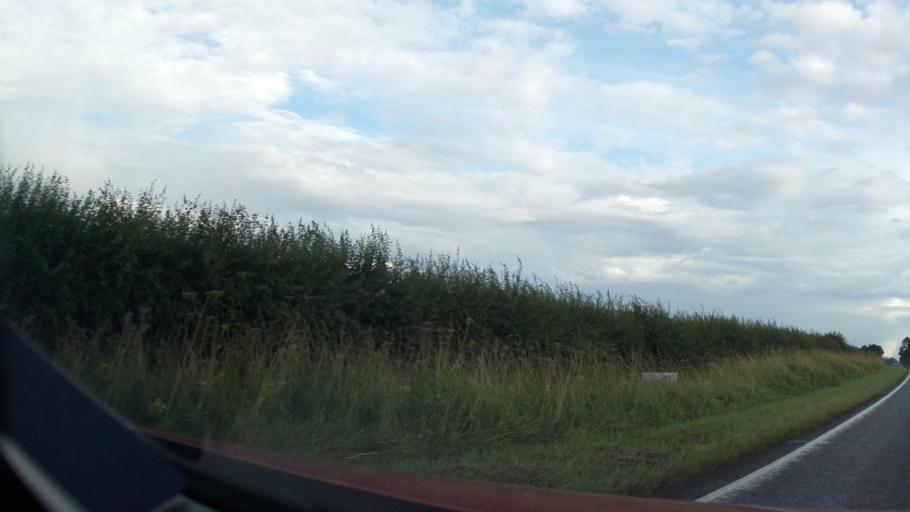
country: GB
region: England
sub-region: Oxfordshire
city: Woodstock
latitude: 51.8792
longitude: -1.3292
